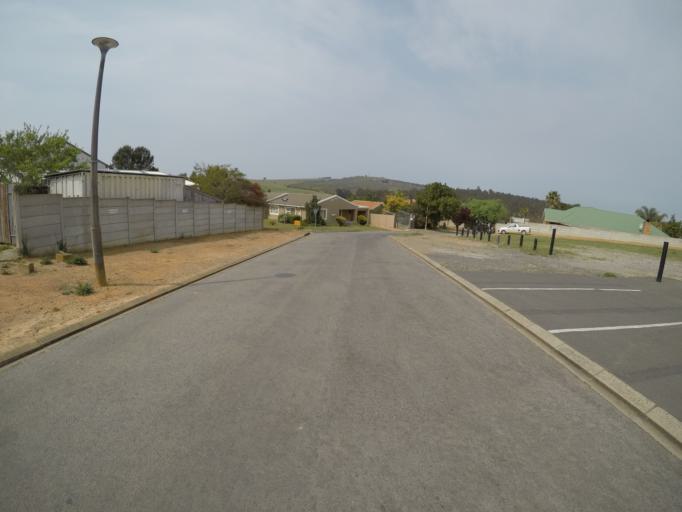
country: ZA
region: Western Cape
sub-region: West Coast District Municipality
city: Malmesbury
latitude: -33.4602
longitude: 18.7416
